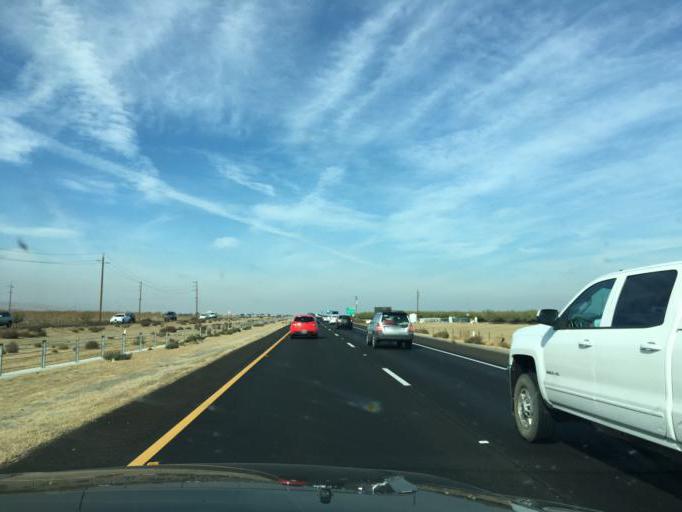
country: US
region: California
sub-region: Fresno County
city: Huron
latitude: 36.2378
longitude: -120.2334
